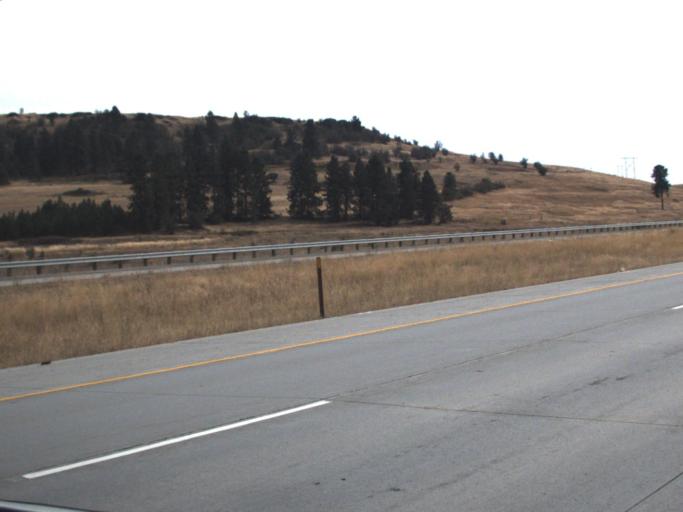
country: US
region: Washington
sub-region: Spokane County
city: Mead
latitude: 47.7466
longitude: -117.3601
